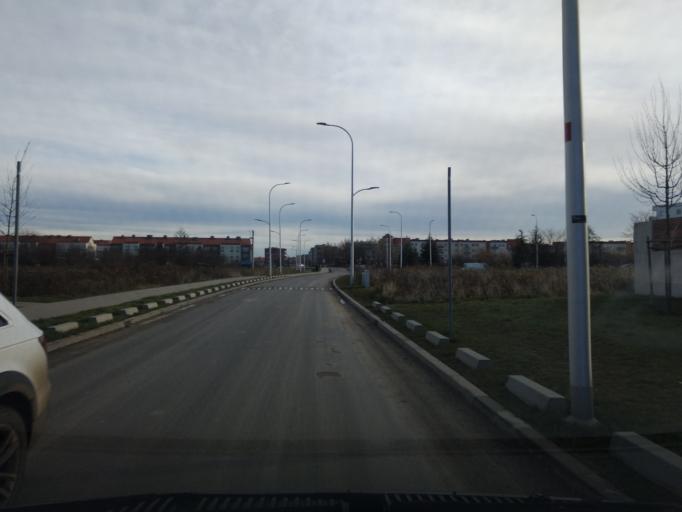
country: PL
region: Lower Silesian Voivodeship
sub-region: Powiat wroclawski
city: Zerniki Wroclawskie
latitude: 51.0538
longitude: 17.0550
